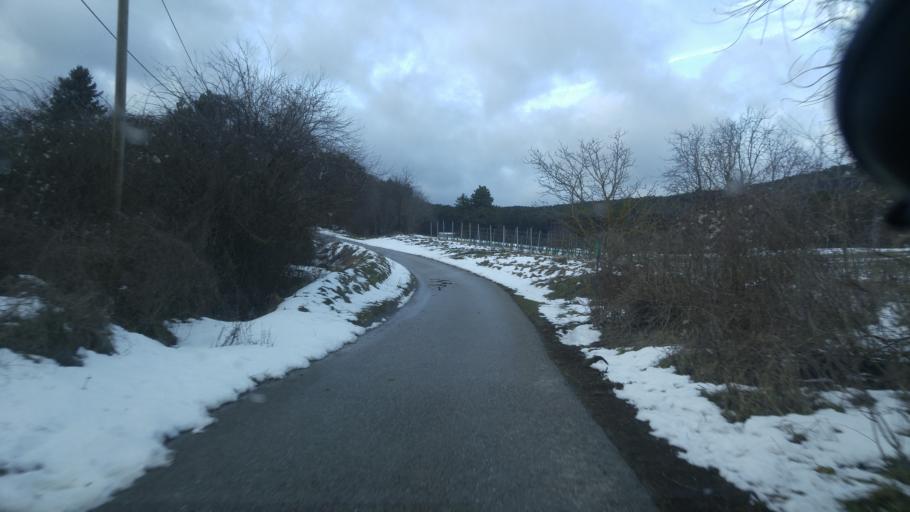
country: AT
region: Lower Austria
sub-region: Politischer Bezirk Baden
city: Bad Voslau
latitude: 47.9633
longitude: 16.1817
